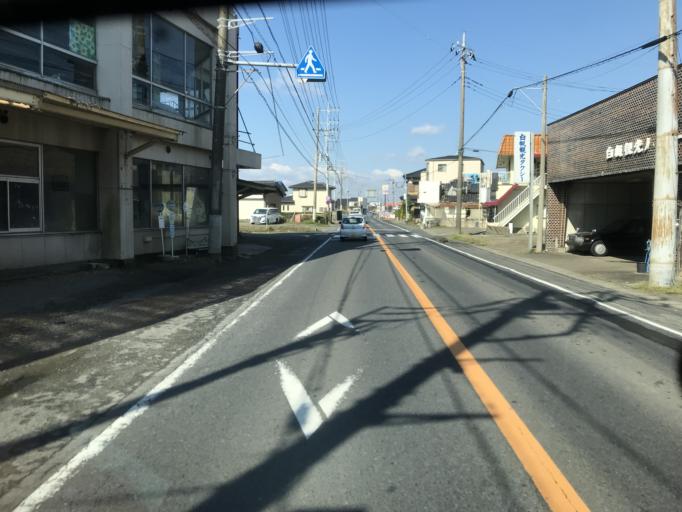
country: JP
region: Ibaraki
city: Itako
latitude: 35.9856
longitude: 140.4863
